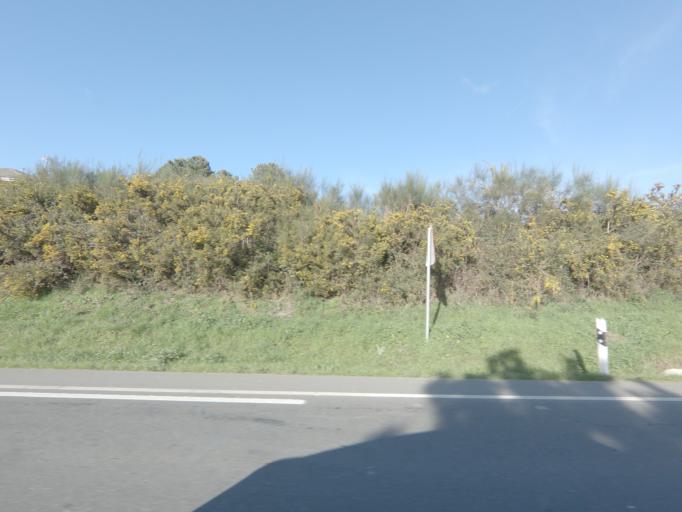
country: ES
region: Galicia
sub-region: Provincia de Pontevedra
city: Silleda
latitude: 42.7094
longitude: -8.2717
